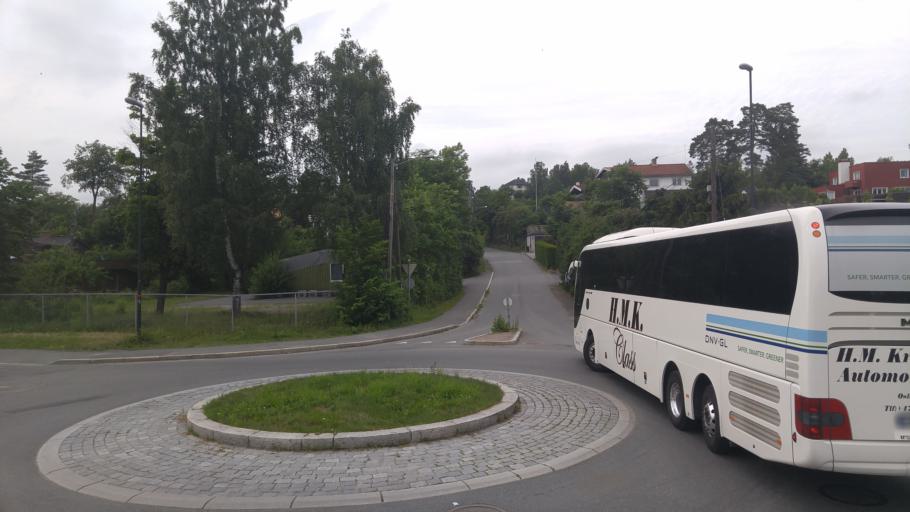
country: NO
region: Akershus
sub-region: Baerum
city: Sandvika
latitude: 59.8931
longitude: 10.5554
